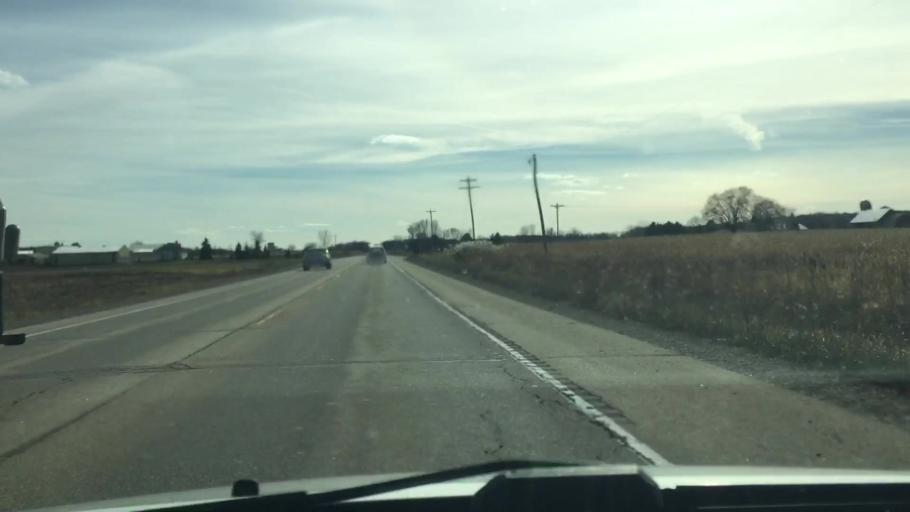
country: US
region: Wisconsin
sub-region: Brown County
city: Pulaski
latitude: 44.6300
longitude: -88.2202
